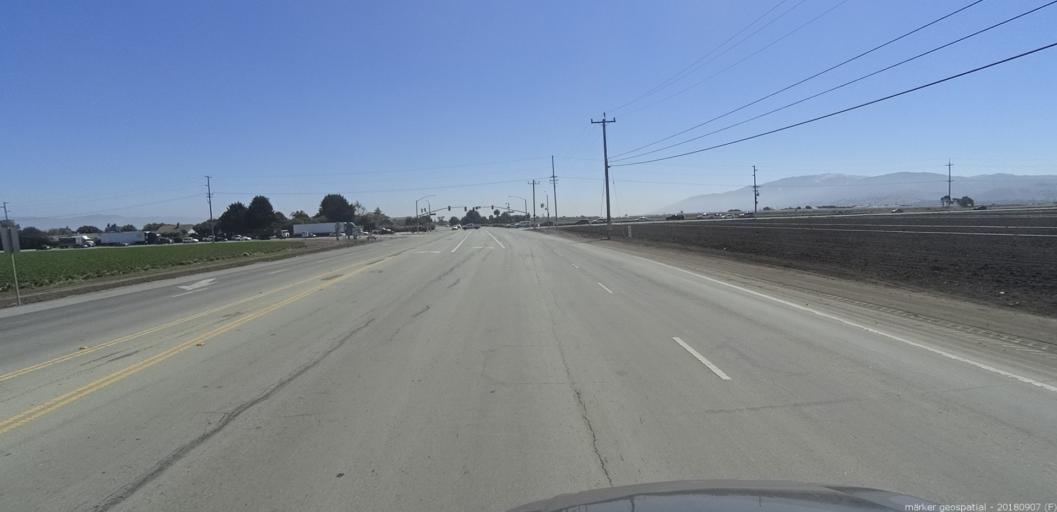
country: US
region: California
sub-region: Monterey County
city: Salinas
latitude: 36.6676
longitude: -121.6867
